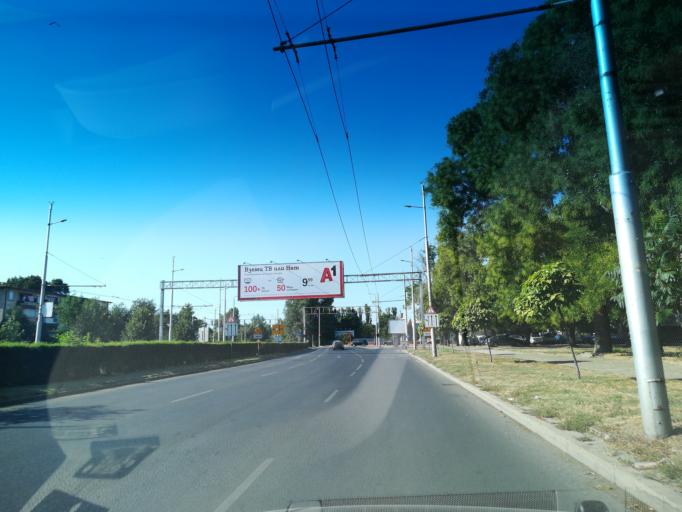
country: BG
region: Plovdiv
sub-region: Obshtina Plovdiv
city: Plovdiv
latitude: 42.1603
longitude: 24.7304
